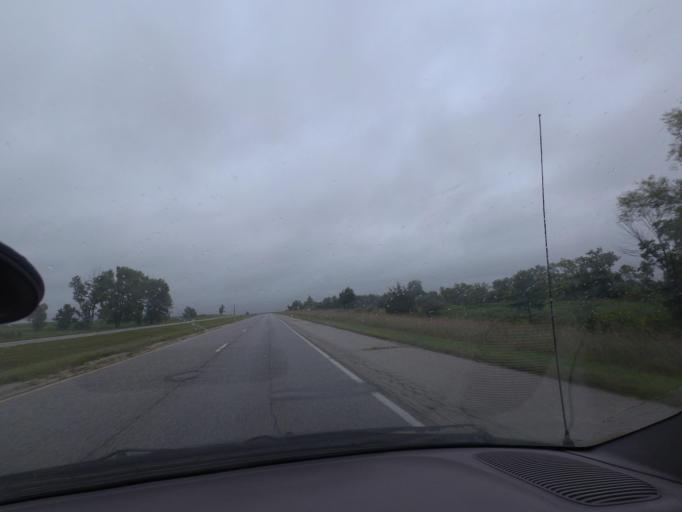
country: US
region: Illinois
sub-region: Pike County
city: Pittsfield
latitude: 39.6706
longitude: -90.8091
